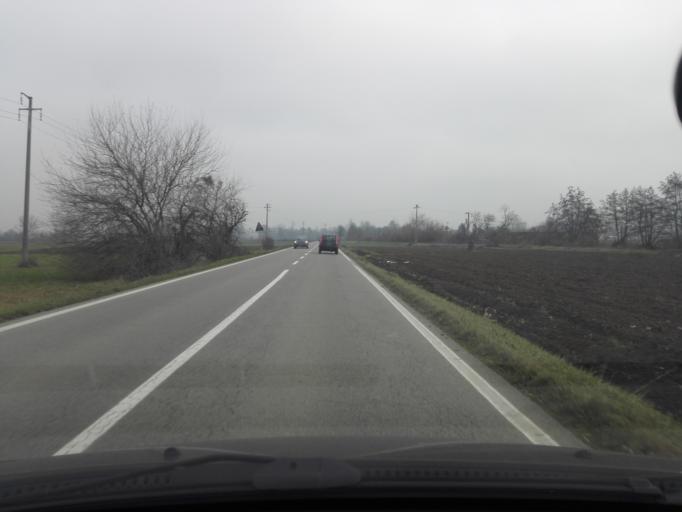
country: IT
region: Piedmont
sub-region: Provincia di Alessandria
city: Bosco Marengo
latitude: 44.8261
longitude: 8.6636
